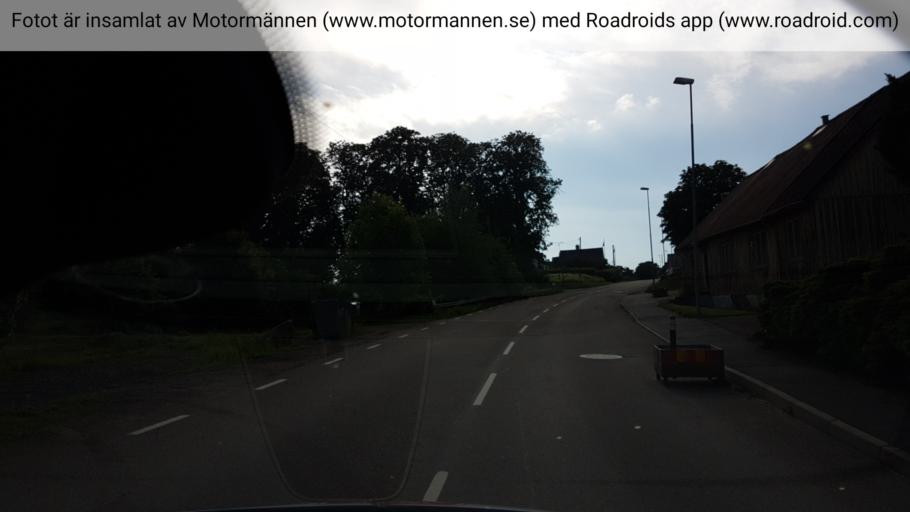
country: SE
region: Skane
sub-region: Astorps Kommun
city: Kvidinge
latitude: 56.1284
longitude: 13.0842
